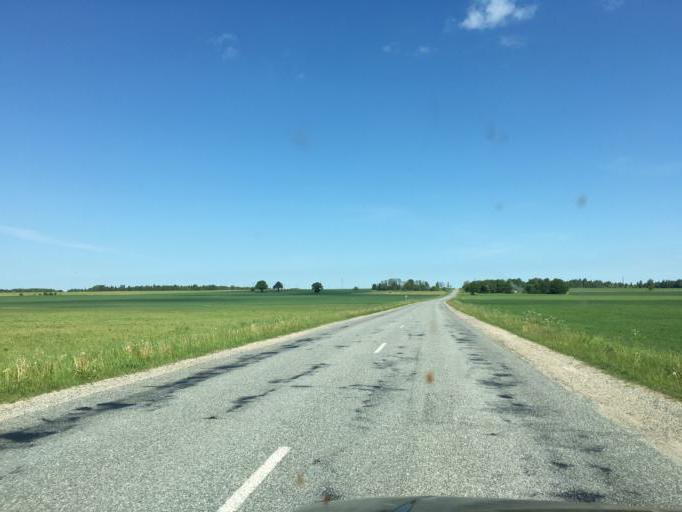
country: LV
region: Talsu Rajons
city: Valdemarpils
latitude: 57.3491
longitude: 22.4984
